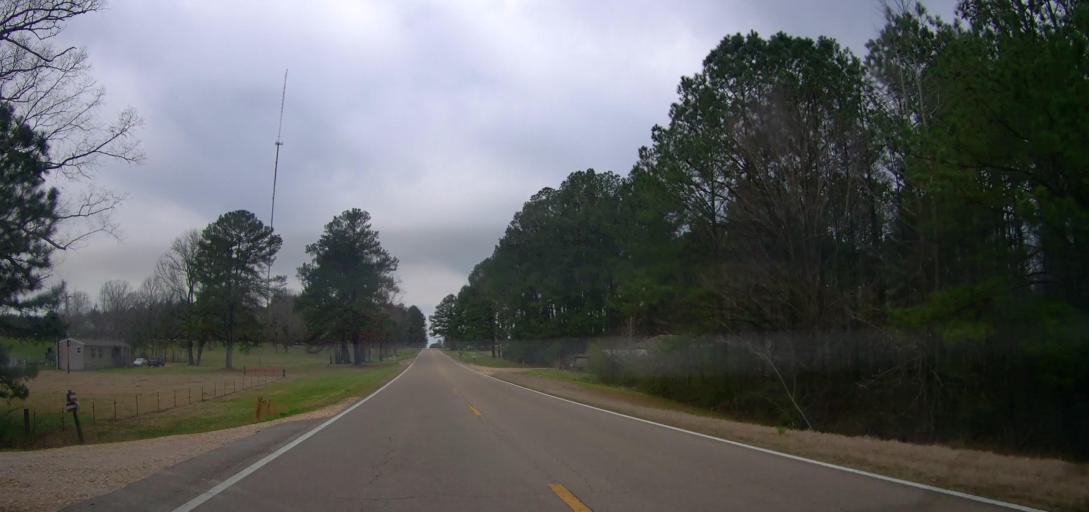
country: US
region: Mississippi
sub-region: Itawamba County
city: Mantachie
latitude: 34.2631
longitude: -88.5350
